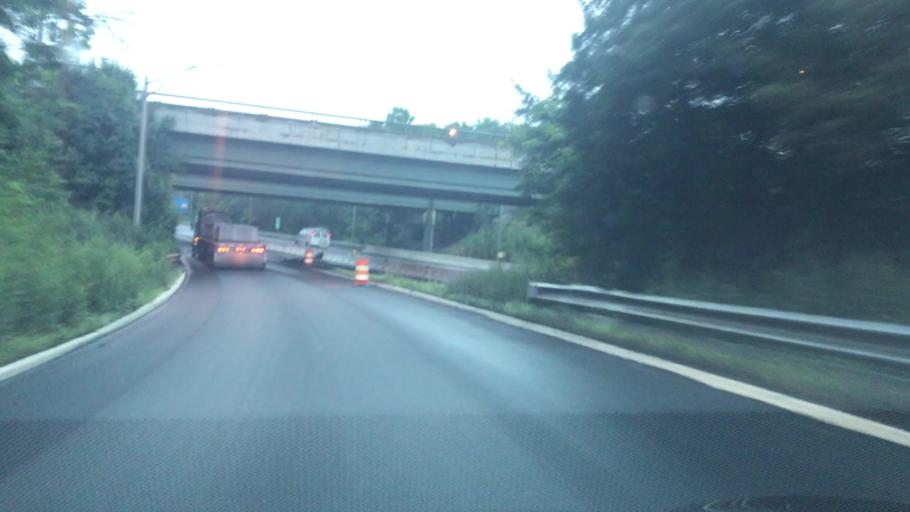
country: US
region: New Jersey
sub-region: Somerset County
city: Bedminster
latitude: 40.6421
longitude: -74.6452
